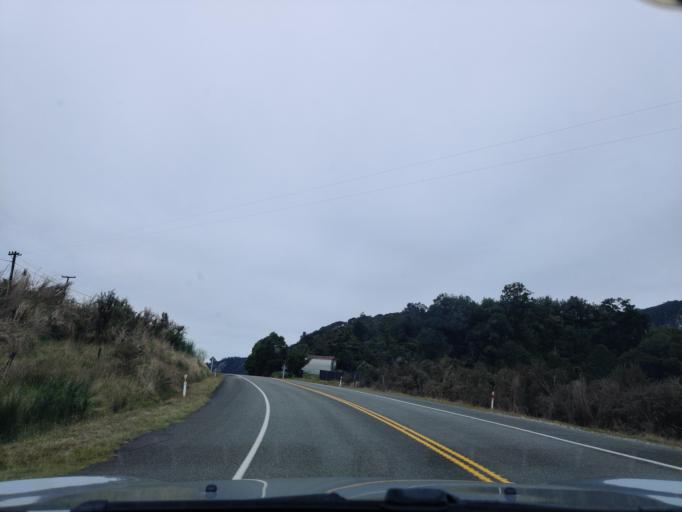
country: NZ
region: West Coast
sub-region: Buller District
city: Westport
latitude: -41.8600
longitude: 171.8596
